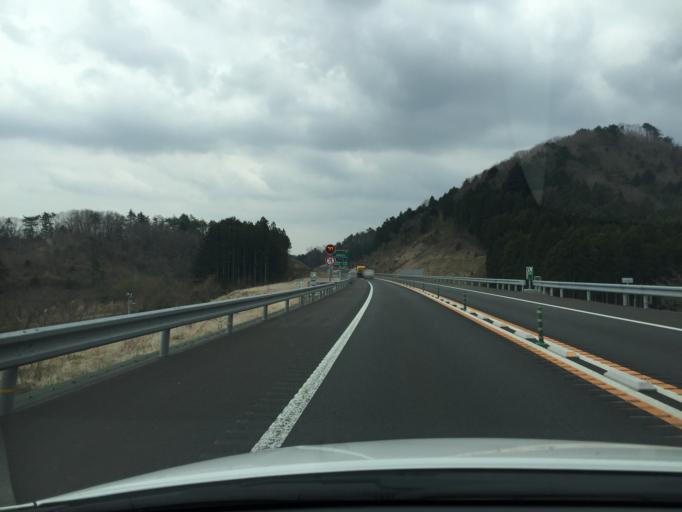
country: JP
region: Miyagi
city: Marumori
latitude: 37.8201
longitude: 140.8751
